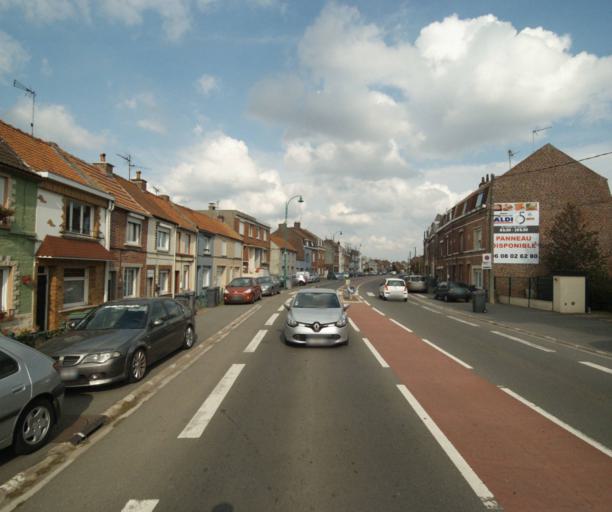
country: FR
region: Nord-Pas-de-Calais
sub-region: Departement du Nord
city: Hallennes-lez-Haubourdin
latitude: 50.6090
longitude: 2.9626
